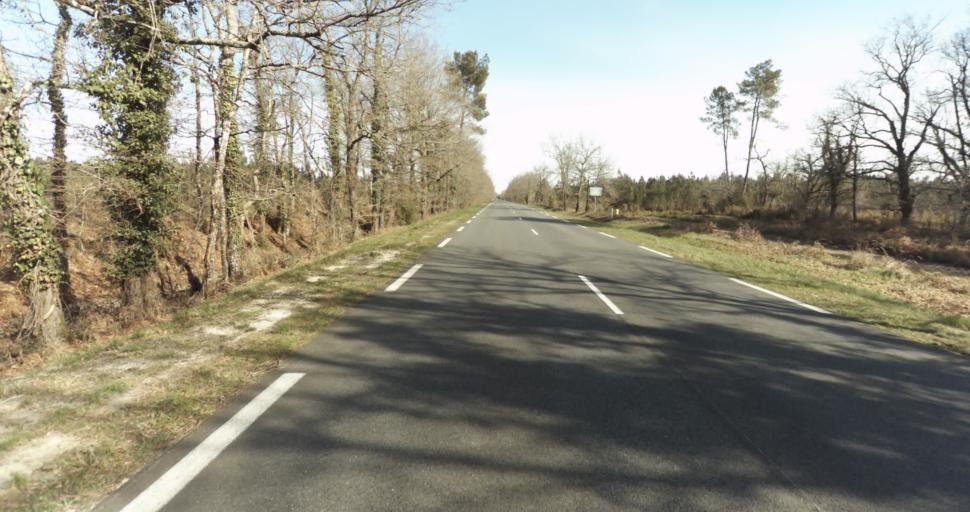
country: FR
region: Aquitaine
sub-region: Departement des Landes
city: Roquefort
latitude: 44.0908
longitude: -0.3093
